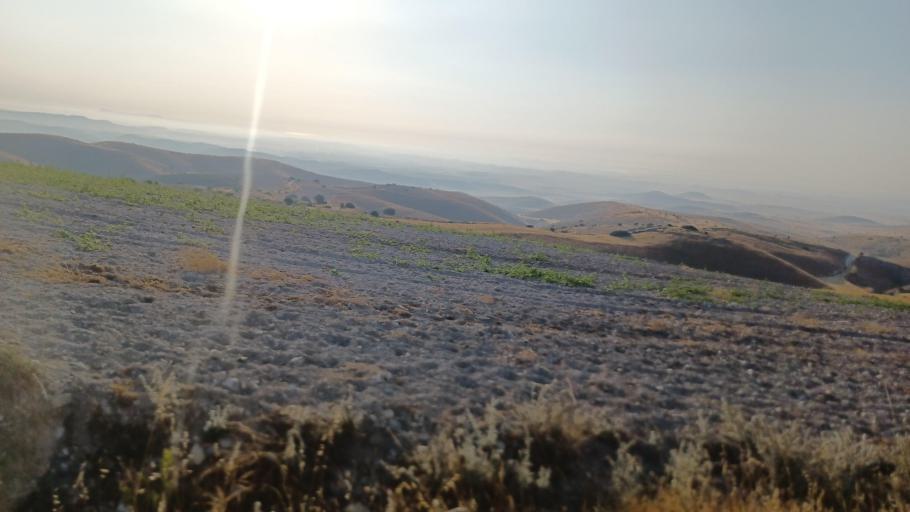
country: CY
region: Larnaka
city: Psevdas
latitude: 34.9193
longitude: 33.4824
